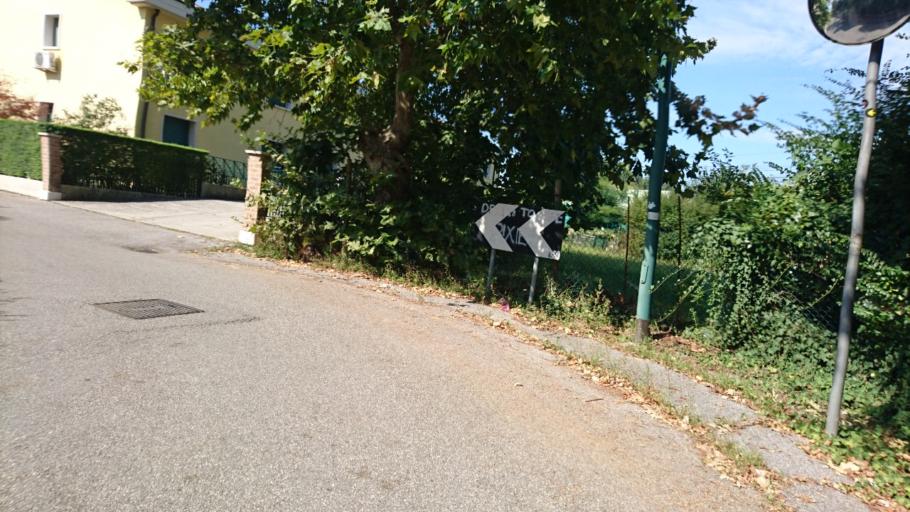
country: IT
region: Veneto
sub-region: Provincia di Venezia
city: Mestre
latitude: 45.5102
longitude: 12.2537
